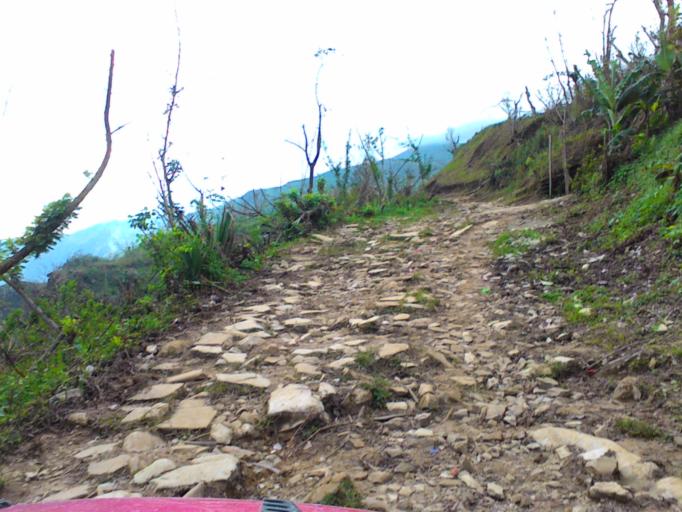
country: HT
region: Grandans
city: Moron
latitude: 18.4578
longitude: -74.1162
